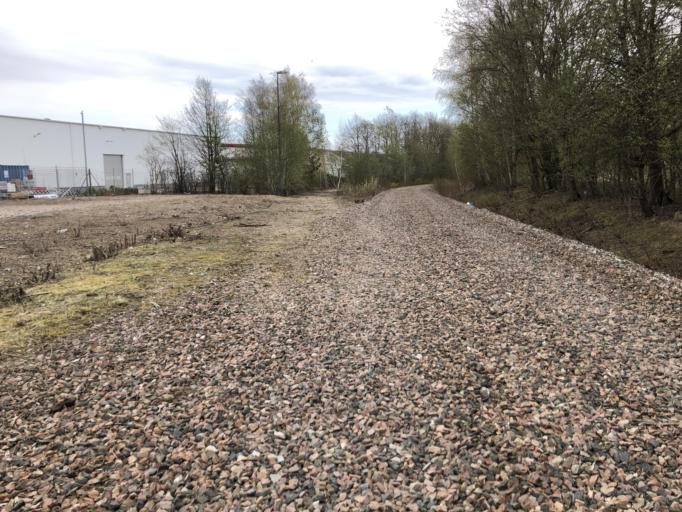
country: SE
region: Skane
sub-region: Malmo
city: Tygelsjo
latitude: 55.5532
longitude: 13.0387
